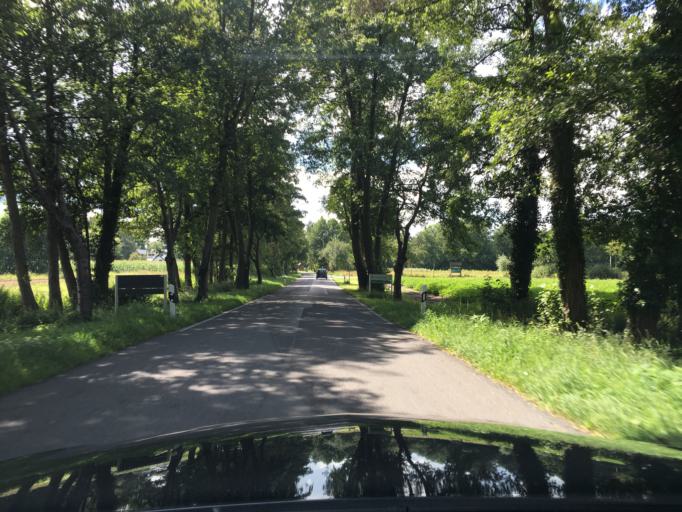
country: DE
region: Brandenburg
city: Burg
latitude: 51.8514
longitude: 14.1045
